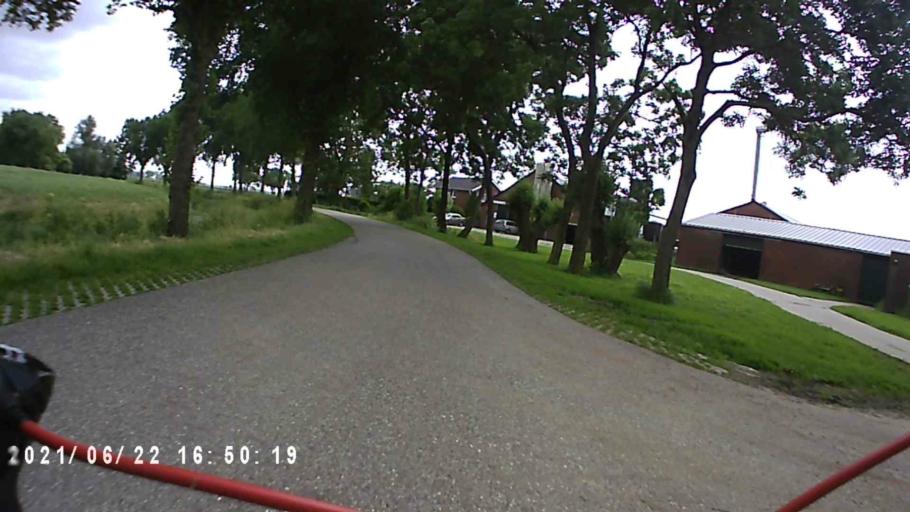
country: NL
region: Groningen
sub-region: Gemeente Bedum
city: Bedum
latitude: 53.3323
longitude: 6.6371
